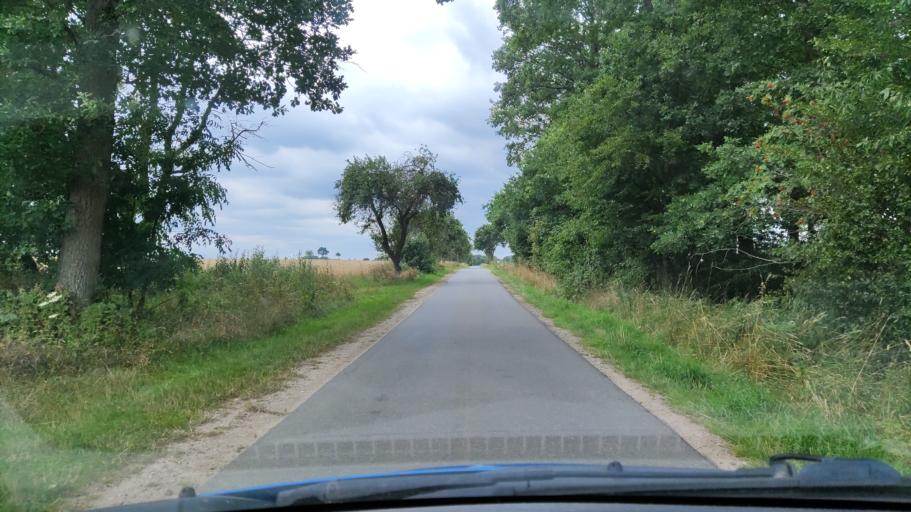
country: DE
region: Lower Saxony
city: Romstedt
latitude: 53.1052
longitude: 10.6679
